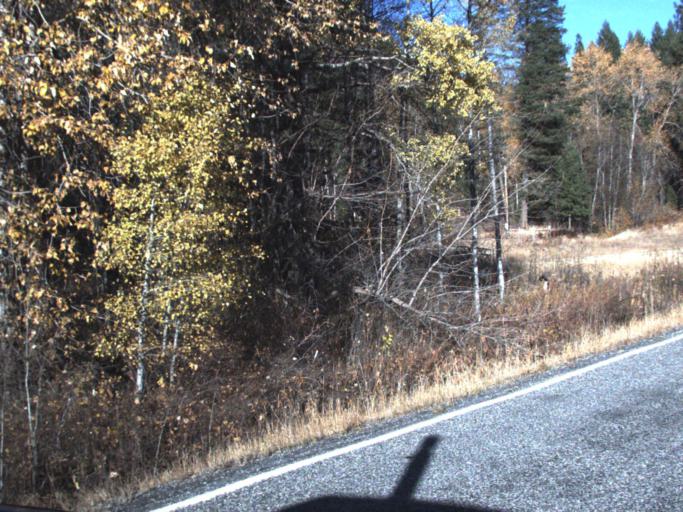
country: US
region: Washington
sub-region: Ferry County
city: Republic
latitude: 48.4464
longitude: -118.7437
